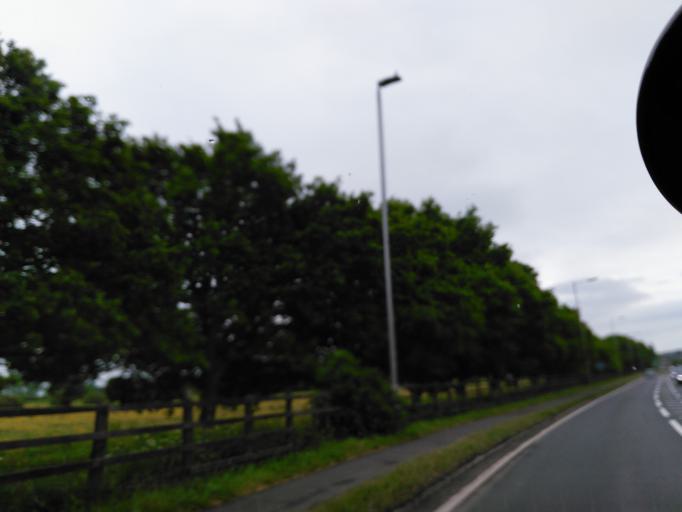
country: GB
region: England
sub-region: Somerset
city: Street
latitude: 51.1360
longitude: -2.7352
